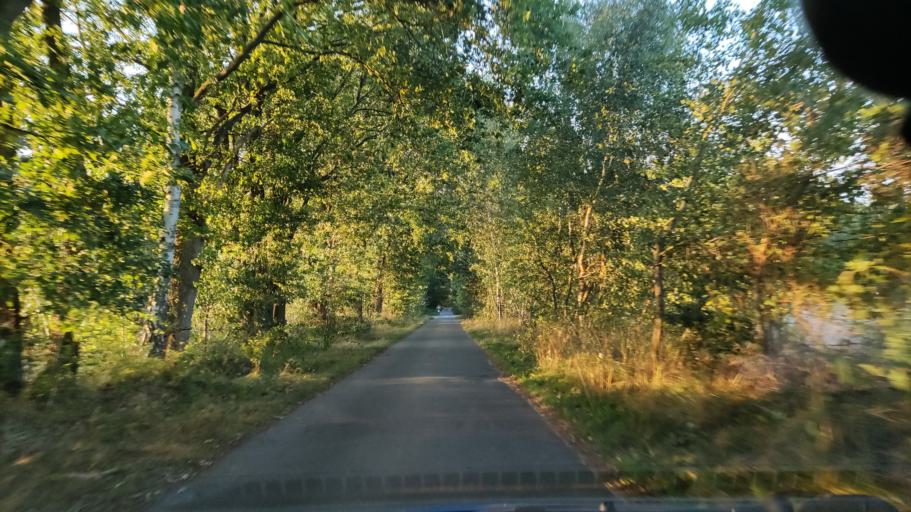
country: DE
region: Lower Saxony
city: Eimke
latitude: 52.9683
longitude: 10.3573
